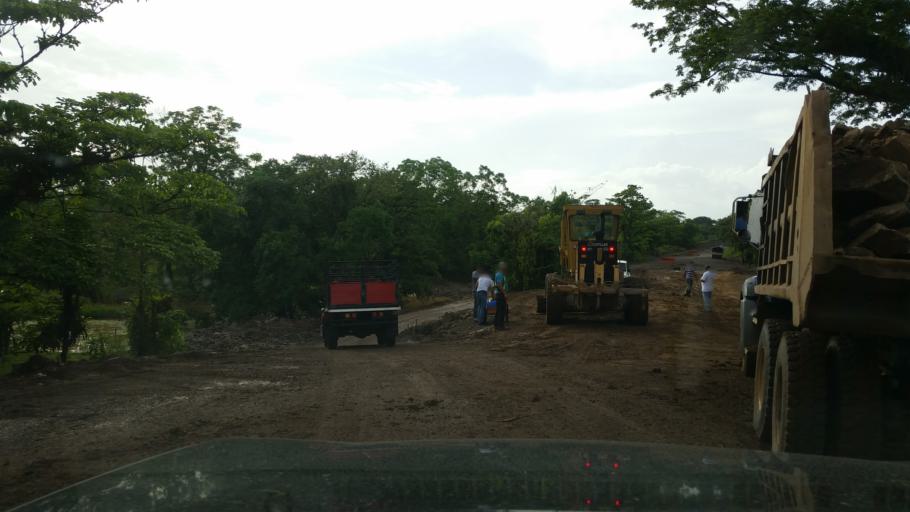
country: NI
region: Matagalpa
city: Rio Blanco
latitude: 13.0818
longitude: -85.0609
